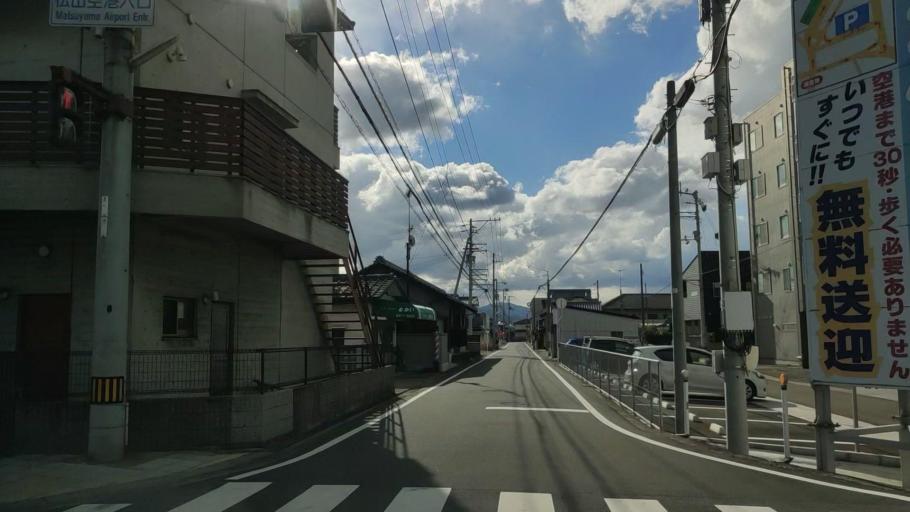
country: JP
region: Ehime
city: Masaki-cho
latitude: 33.8283
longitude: 132.7086
